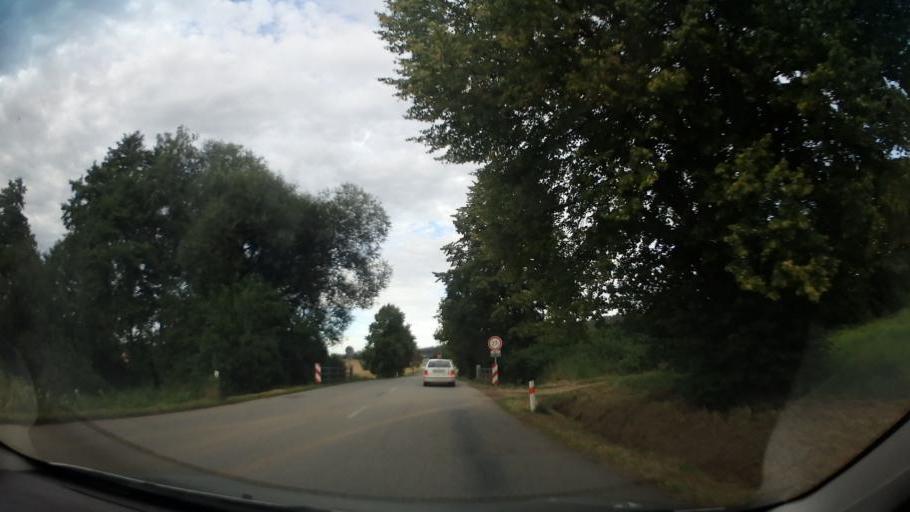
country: CZ
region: South Moravian
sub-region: Okres Blansko
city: Boskovice
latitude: 49.5431
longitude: 16.7046
